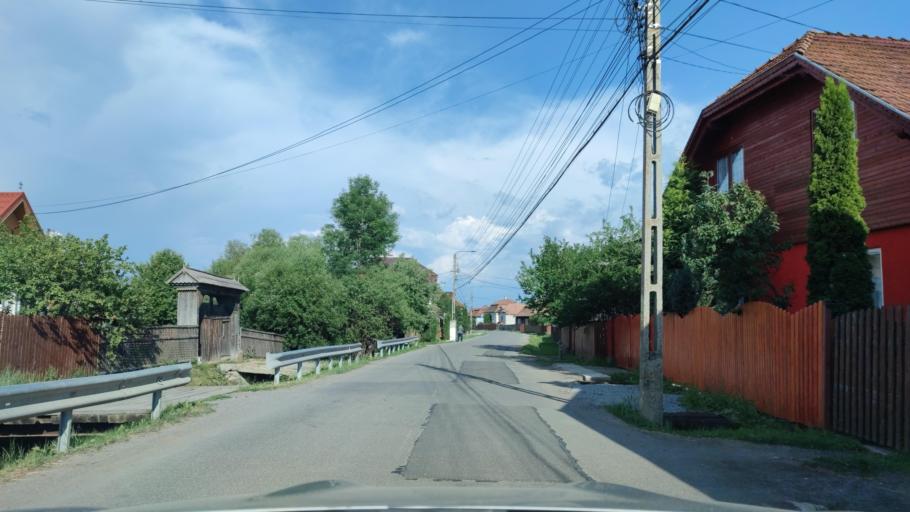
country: RO
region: Harghita
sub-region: Comuna Remetea
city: Remetea
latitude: 46.7948
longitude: 25.4369
